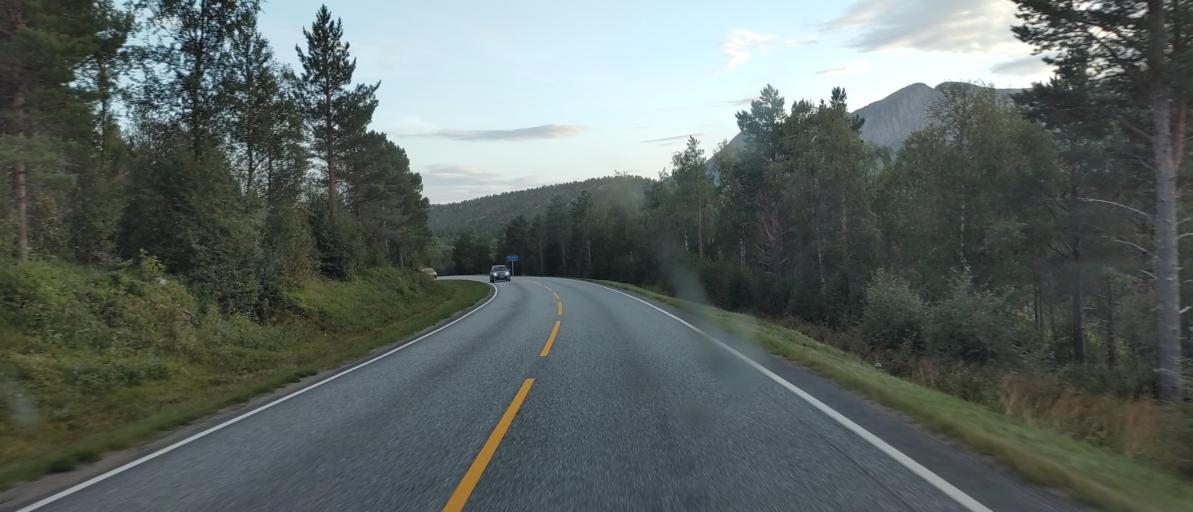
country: NO
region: Nordland
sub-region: Lodingen
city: Lodingen
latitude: 68.2067
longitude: 16.0598
